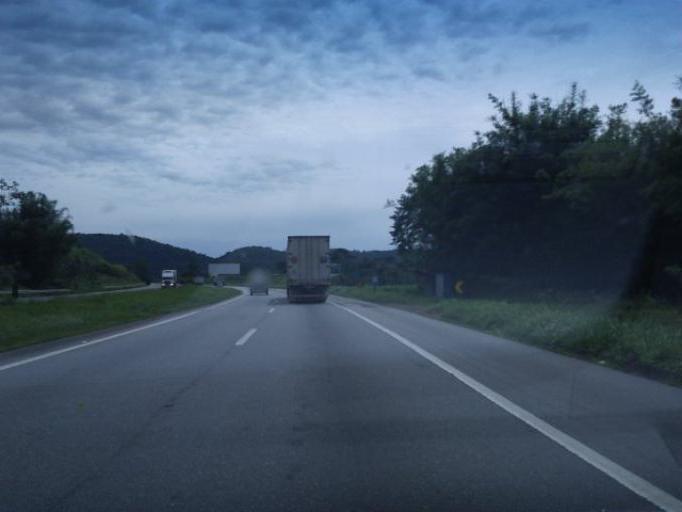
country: BR
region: Sao Paulo
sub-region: Miracatu
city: Miracatu
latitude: -24.1988
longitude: -47.3690
